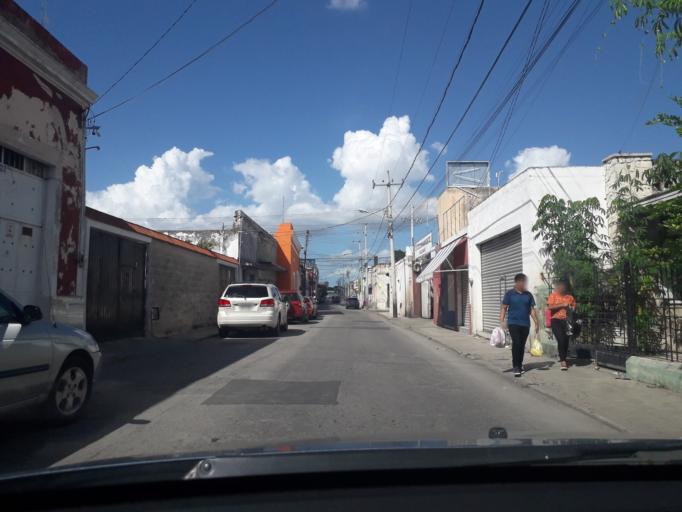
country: MX
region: Yucatan
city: Merida
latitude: 20.9592
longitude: -89.6220
